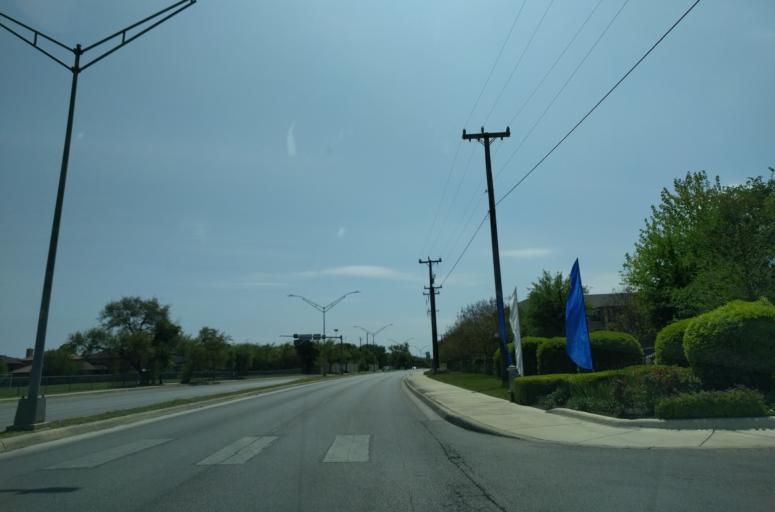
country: US
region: Texas
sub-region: Bexar County
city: Shavano Park
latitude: 29.5752
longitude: -98.5858
